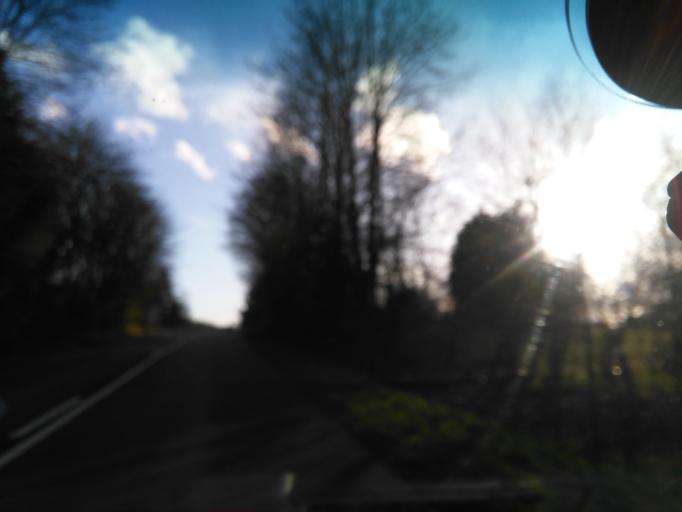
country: FR
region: Lower Normandy
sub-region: Departement du Calvados
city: Falaise
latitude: 48.8650
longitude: -0.2223
